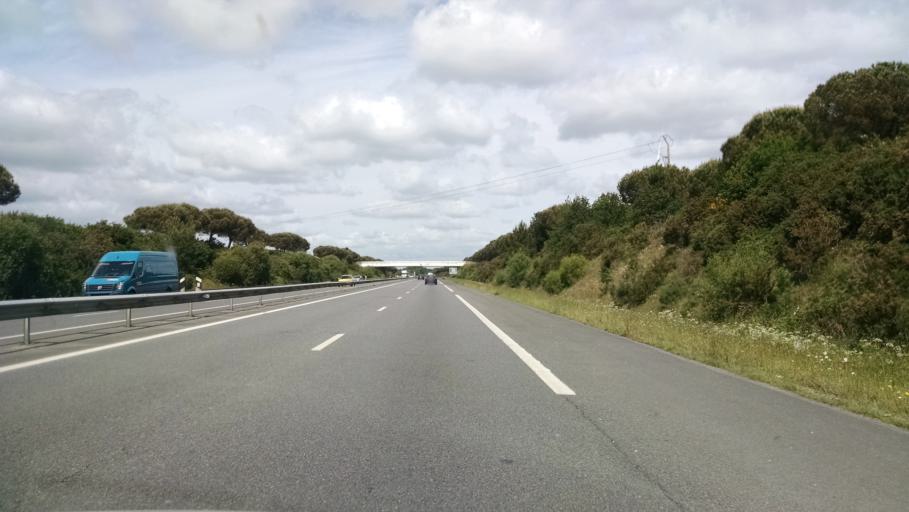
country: FR
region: Pays de la Loire
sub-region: Departement de la Loire-Atlantique
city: Prinquiau
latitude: 47.4120
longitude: -2.0215
